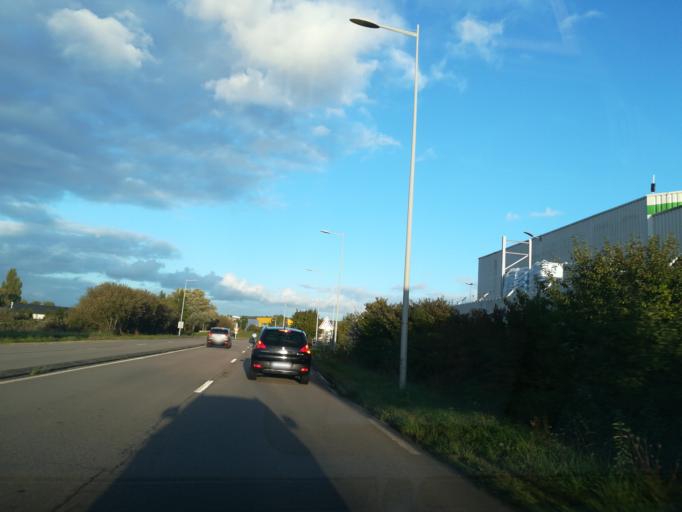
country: FR
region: Haute-Normandie
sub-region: Departement de la Seine-Maritime
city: Oissel
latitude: 49.3310
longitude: 1.0891
